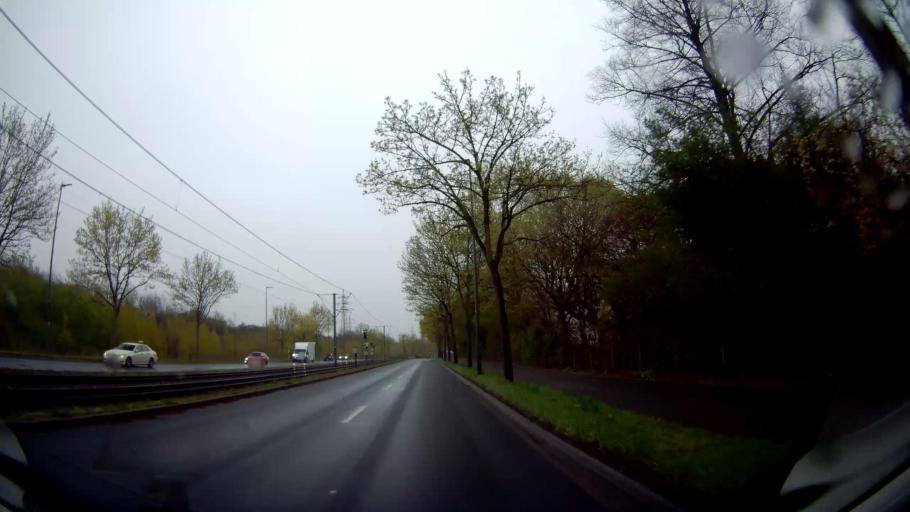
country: DE
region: North Rhine-Westphalia
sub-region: Regierungsbezirk Arnsberg
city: Dortmund
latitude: 51.5283
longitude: 7.4218
